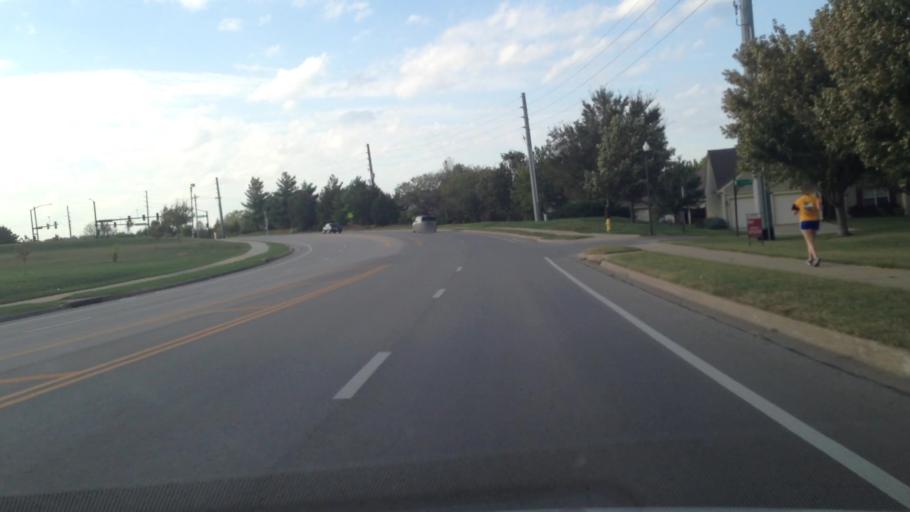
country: US
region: Kansas
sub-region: Douglas County
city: Lawrence
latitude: 38.9585
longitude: -95.3232
